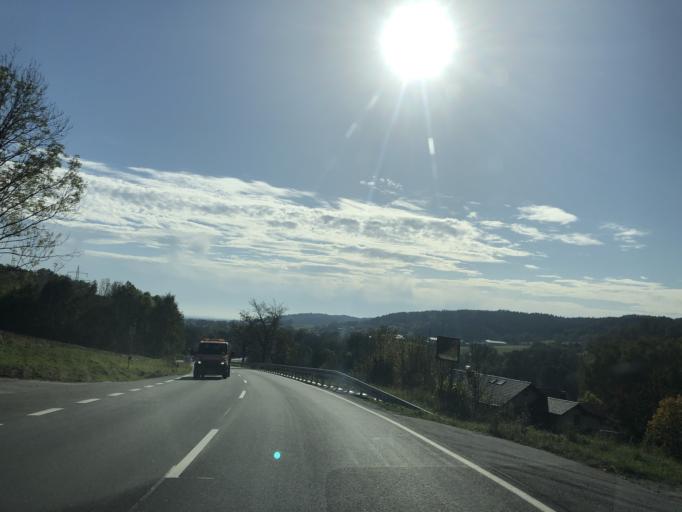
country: DE
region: Bavaria
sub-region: Lower Bavaria
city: Grafling
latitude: 48.8854
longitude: 12.9666
